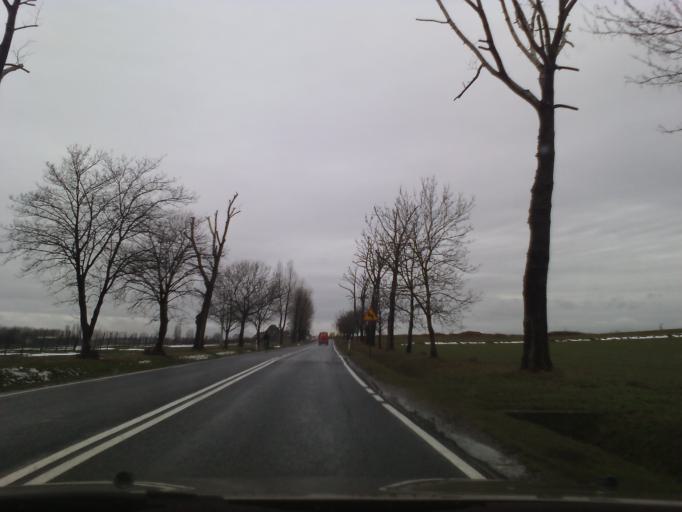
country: PL
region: Lower Silesian Voivodeship
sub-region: Powiat swidnicki
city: Swiebodzice
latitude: 50.8480
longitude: 16.3786
